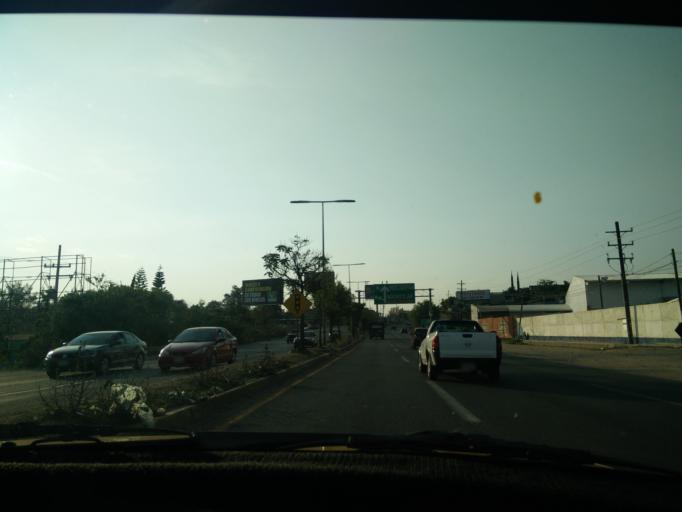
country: MX
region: Oaxaca
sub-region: Santa Maria Atzompa
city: Fraccionamiento Riberas de San Jeronimo
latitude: 17.1335
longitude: -96.7732
